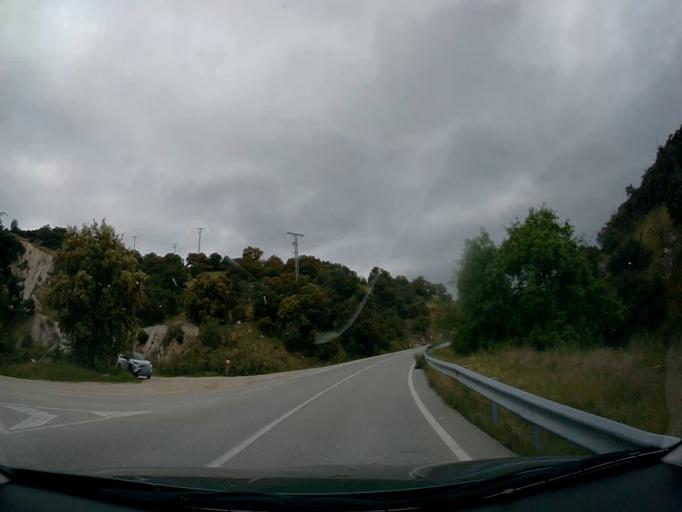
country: ES
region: Madrid
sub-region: Provincia de Madrid
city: Navalagamella
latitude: 40.4423
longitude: -4.1157
